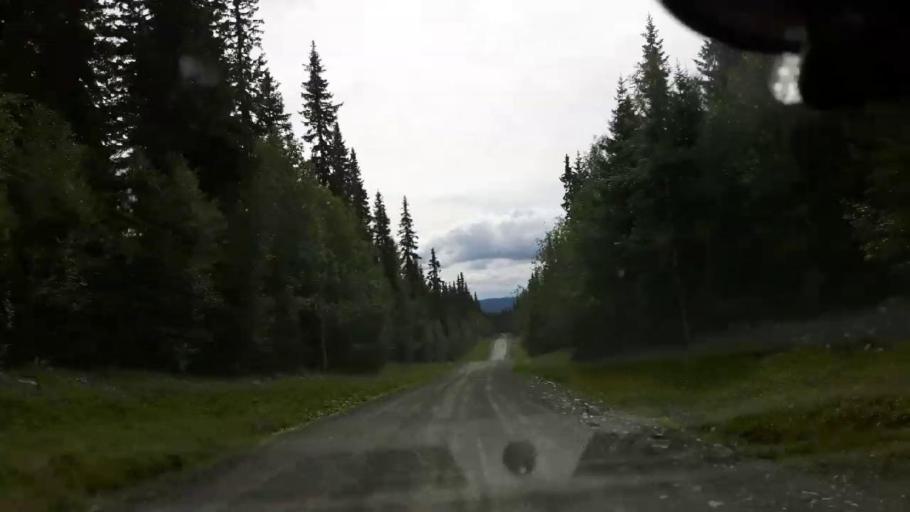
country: SE
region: Jaemtland
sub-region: Krokoms Kommun
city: Valla
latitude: 63.7182
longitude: 13.8583
